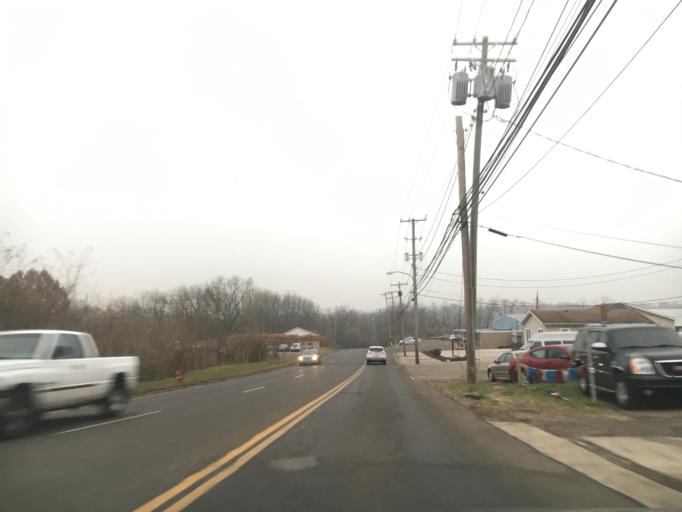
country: US
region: Ohio
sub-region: Summit County
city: Akron
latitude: 41.0911
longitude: -81.4878
